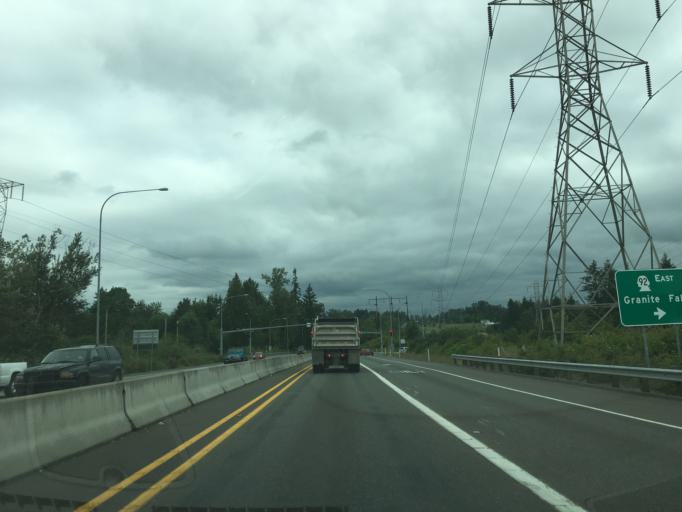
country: US
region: Washington
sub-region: Snohomish County
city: West Lake Stevens
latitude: 48.0266
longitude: -122.1100
